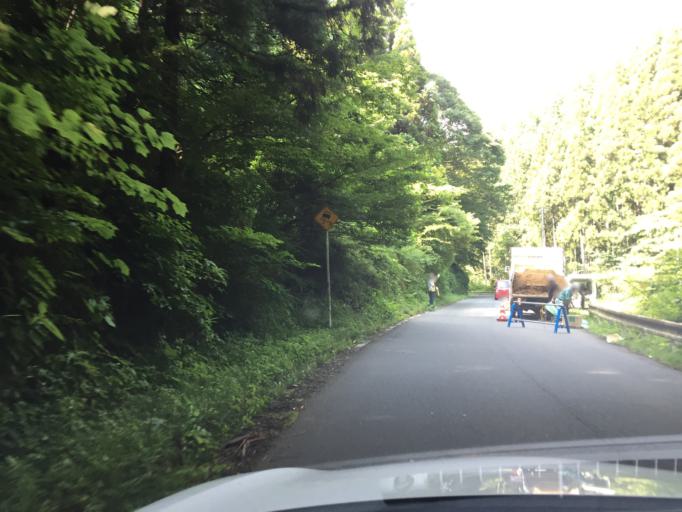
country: JP
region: Fukushima
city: Iwaki
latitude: 36.9964
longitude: 140.7105
